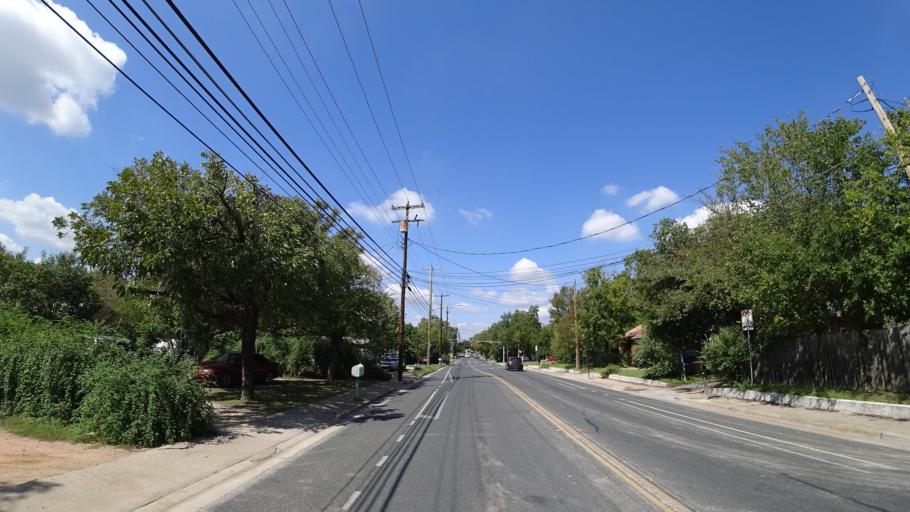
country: US
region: Texas
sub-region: Travis County
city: Austin
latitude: 30.3374
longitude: -97.7136
